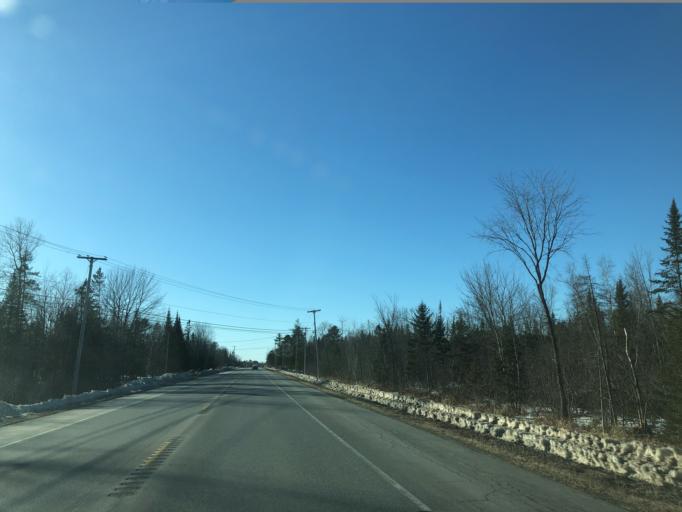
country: US
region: Maine
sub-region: Penobscot County
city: Kenduskeag
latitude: 44.9132
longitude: -68.9082
